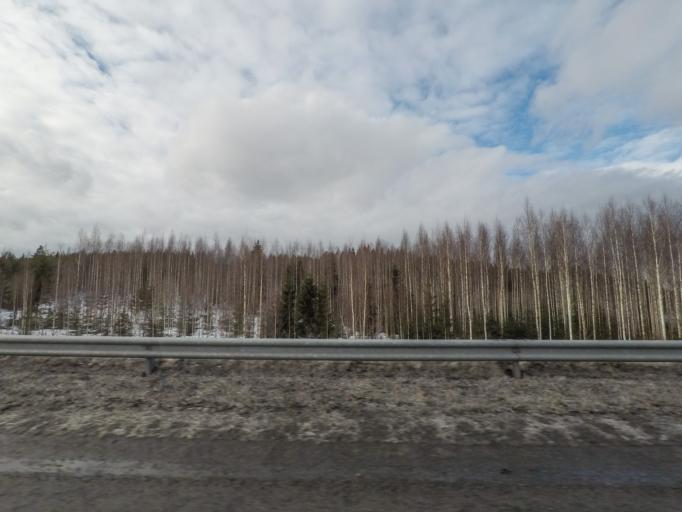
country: FI
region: Southern Savonia
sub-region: Mikkeli
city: Maentyharju
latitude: 61.5392
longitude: 26.8922
